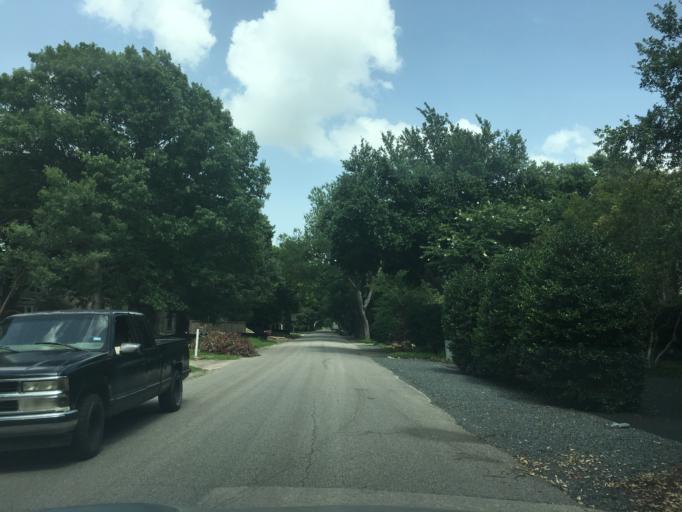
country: US
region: Texas
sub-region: Dallas County
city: University Park
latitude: 32.8863
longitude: -96.8013
